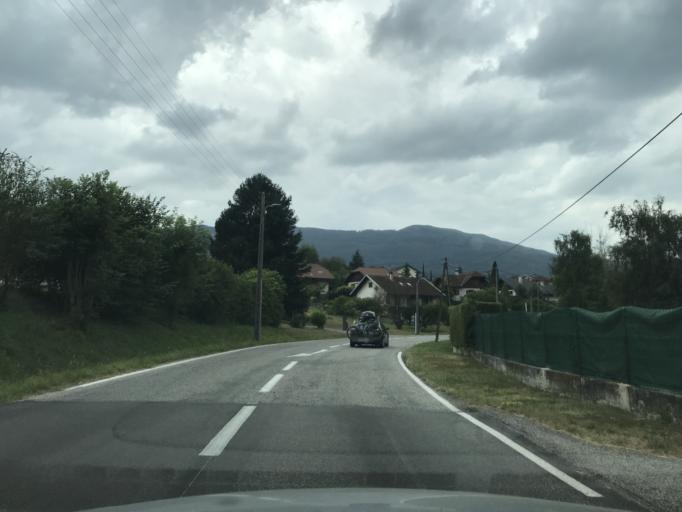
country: FR
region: Rhone-Alpes
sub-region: Departement de la Savoie
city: Brison-Saint-Innocent
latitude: 45.7325
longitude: 5.8881
